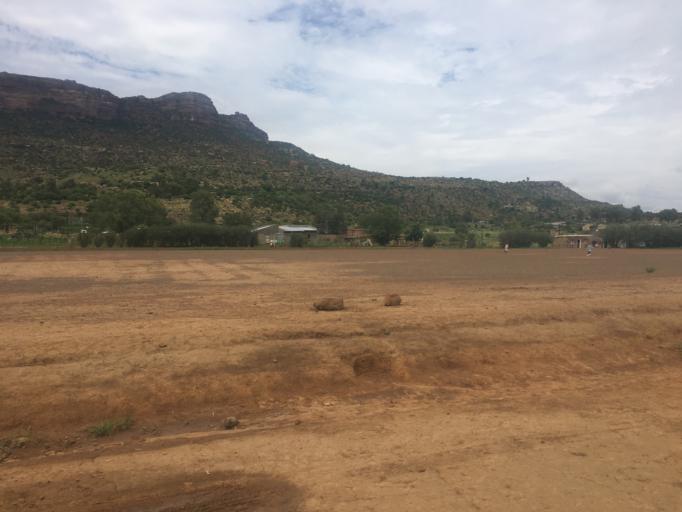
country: LS
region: Maseru
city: Maseru
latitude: -29.3971
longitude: 27.4516
